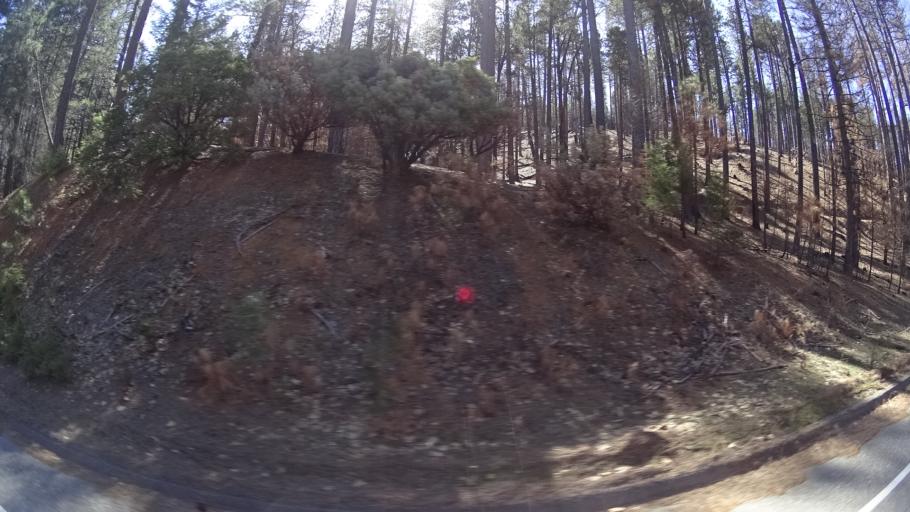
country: US
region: California
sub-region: Tehama County
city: Rancho Tehama Reserve
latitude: 39.6568
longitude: -122.7255
